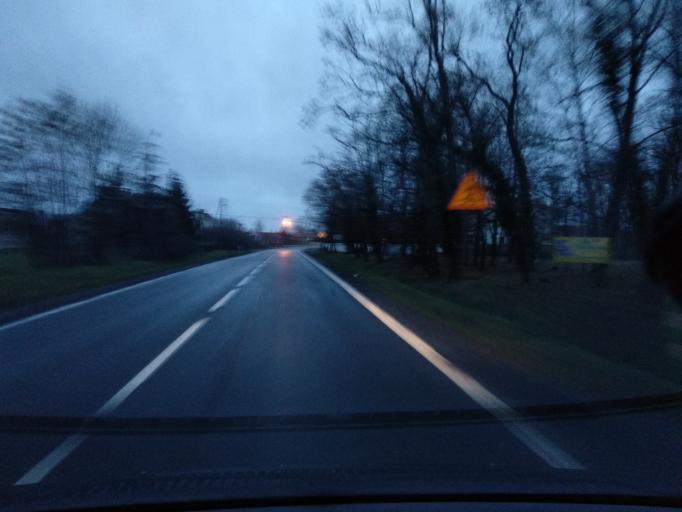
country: PL
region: Lower Silesian Voivodeship
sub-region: Powiat sredzki
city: Malczyce
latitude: 51.2295
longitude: 16.4271
